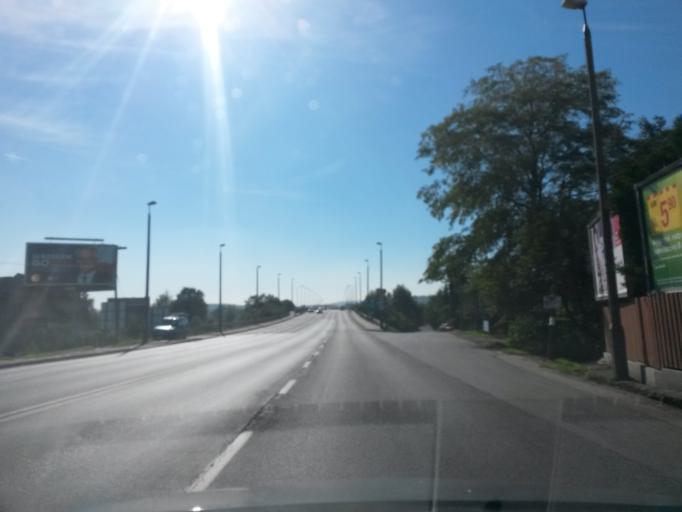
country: PL
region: Lesser Poland Voivodeship
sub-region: Powiat krakowski
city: Libertow
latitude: 49.9957
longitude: 19.9189
